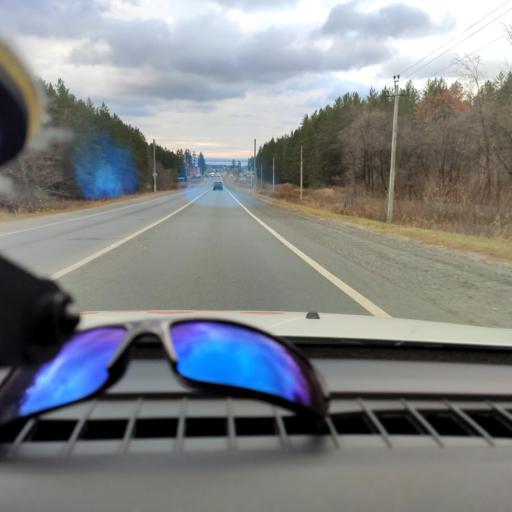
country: RU
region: Samara
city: Volzhskiy
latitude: 53.4433
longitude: 50.1233
